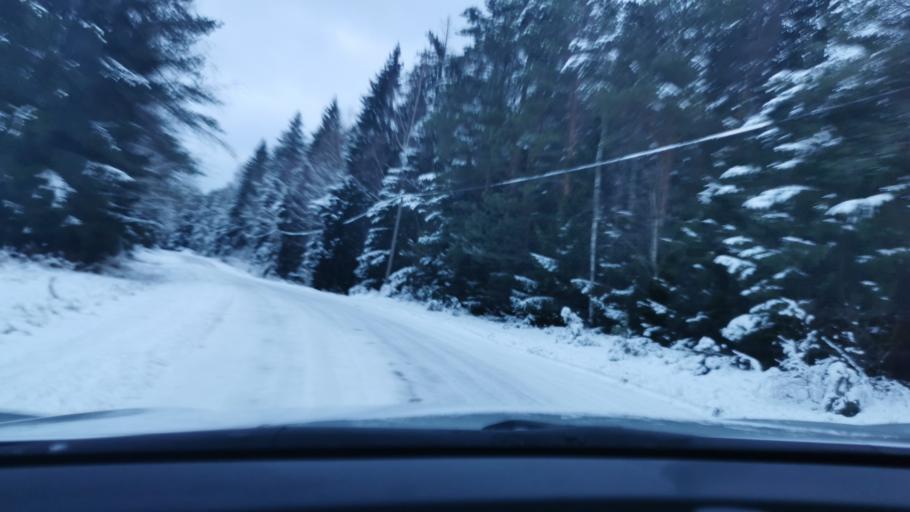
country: EE
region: Laeaene-Virumaa
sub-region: Haljala vald
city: Haljala
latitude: 59.5579
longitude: 26.3206
